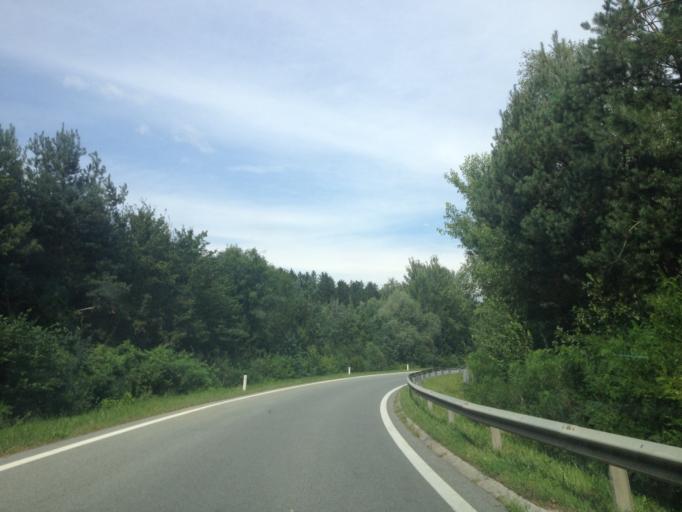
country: AT
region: Burgenland
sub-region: Politischer Bezirk Oberwart
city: Markt Allhau
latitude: 47.2812
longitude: 16.0649
